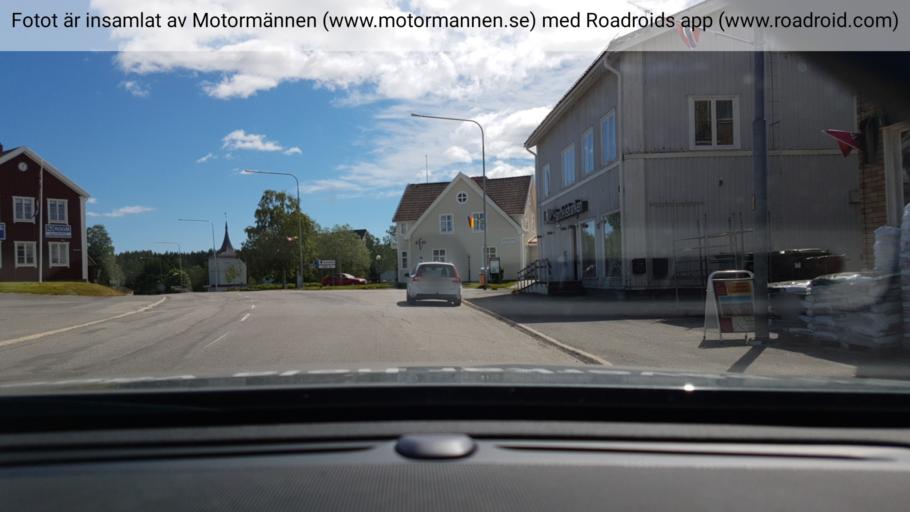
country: SE
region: Vaesterbotten
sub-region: Skelleftea Kommun
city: Burea
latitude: 64.3693
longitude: 21.3145
